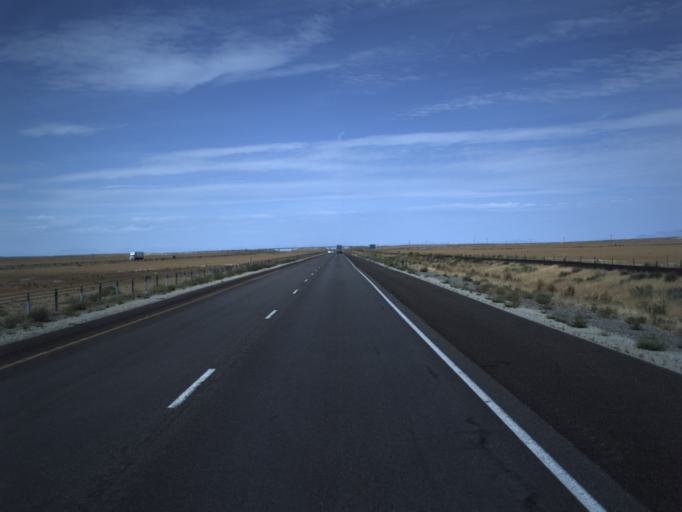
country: US
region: Utah
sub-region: Tooele County
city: Grantsville
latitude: 40.7271
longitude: -113.2379
